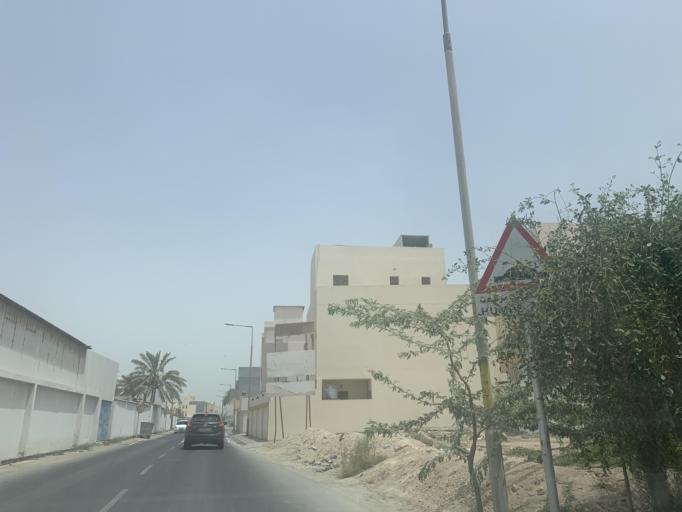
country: BH
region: Manama
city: Jidd Hafs
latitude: 26.2070
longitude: 50.5386
